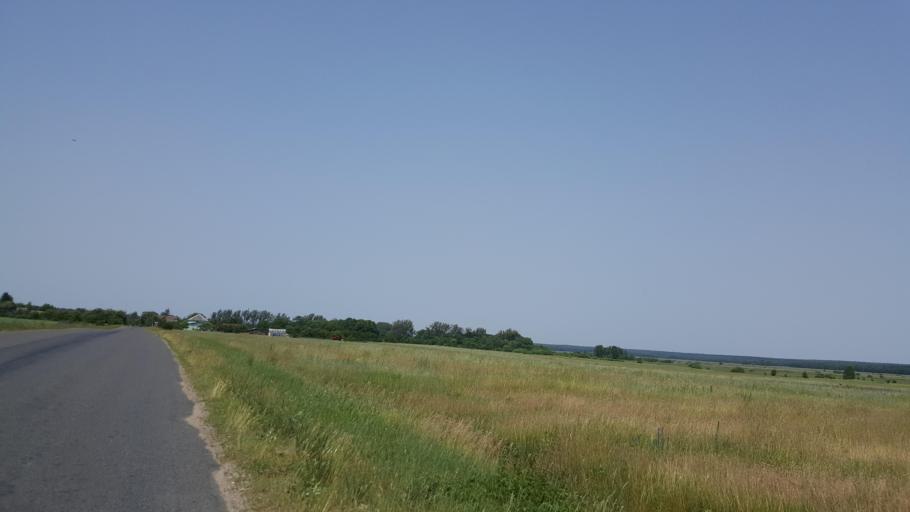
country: BY
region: Brest
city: Kamyanyuki
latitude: 52.4839
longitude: 23.8768
